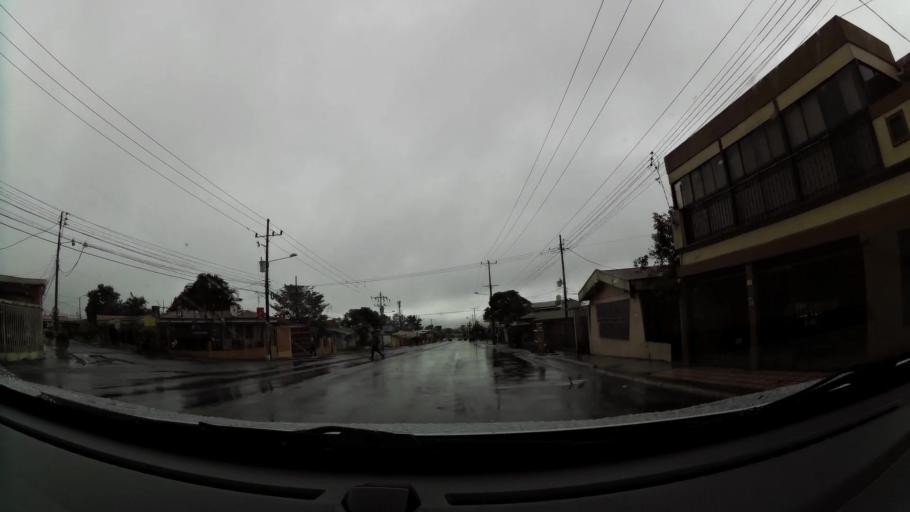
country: CR
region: Cartago
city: Cartago
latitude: 9.8594
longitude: -83.9060
